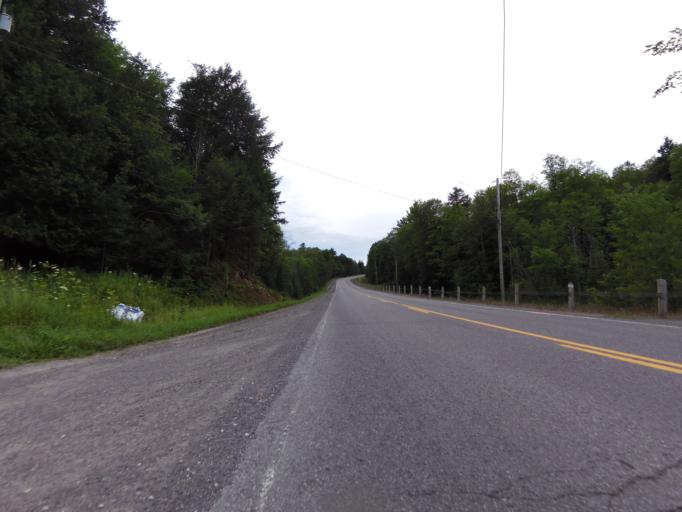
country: CA
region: Ontario
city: Carleton Place
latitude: 45.1104
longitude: -76.3718
